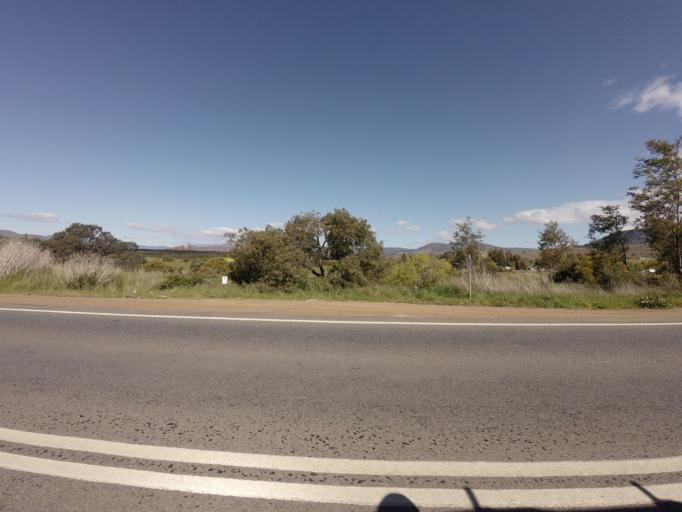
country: AU
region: Tasmania
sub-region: Derwent Valley
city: New Norfolk
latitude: -42.7360
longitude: 146.9584
